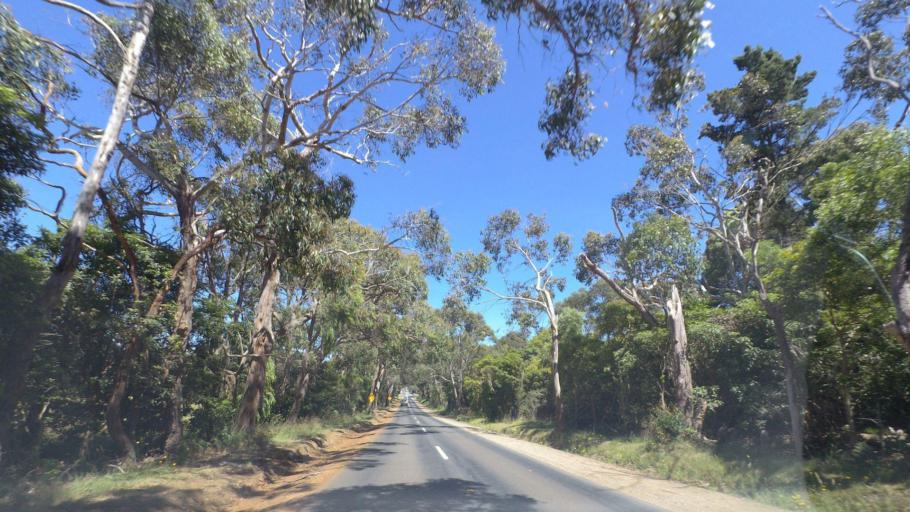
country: AU
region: Victoria
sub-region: Mornington Peninsula
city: Merricks
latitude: -38.3740
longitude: 145.0825
